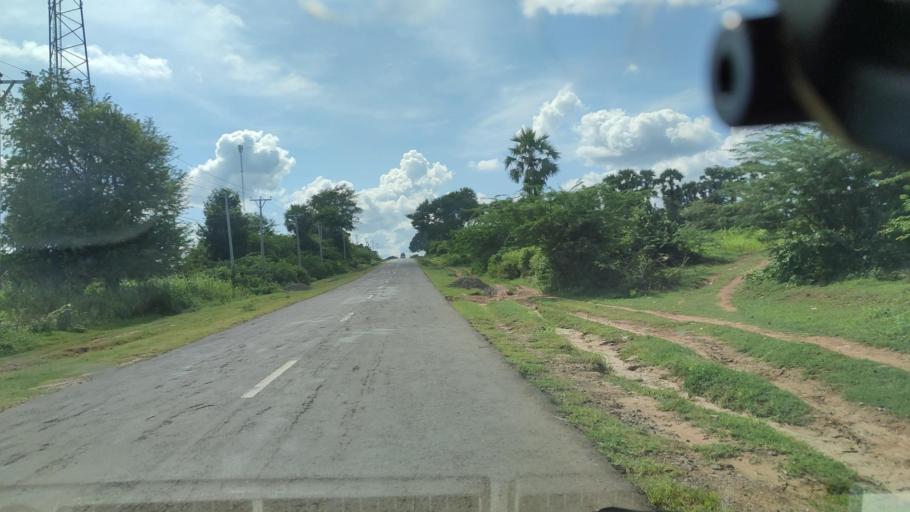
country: MM
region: Mandalay
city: Meiktila
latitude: 20.8194
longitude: 95.6265
